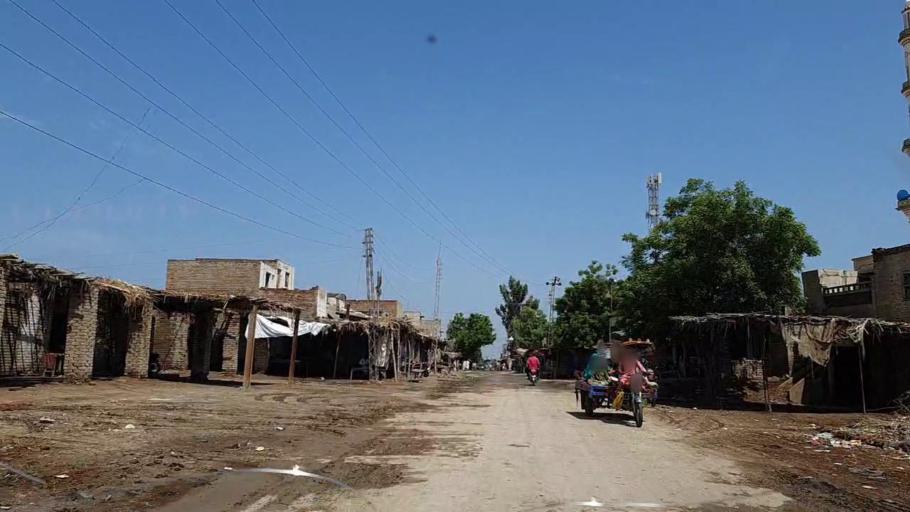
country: PK
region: Sindh
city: Naushahro Firoz
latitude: 26.8111
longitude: 68.1957
